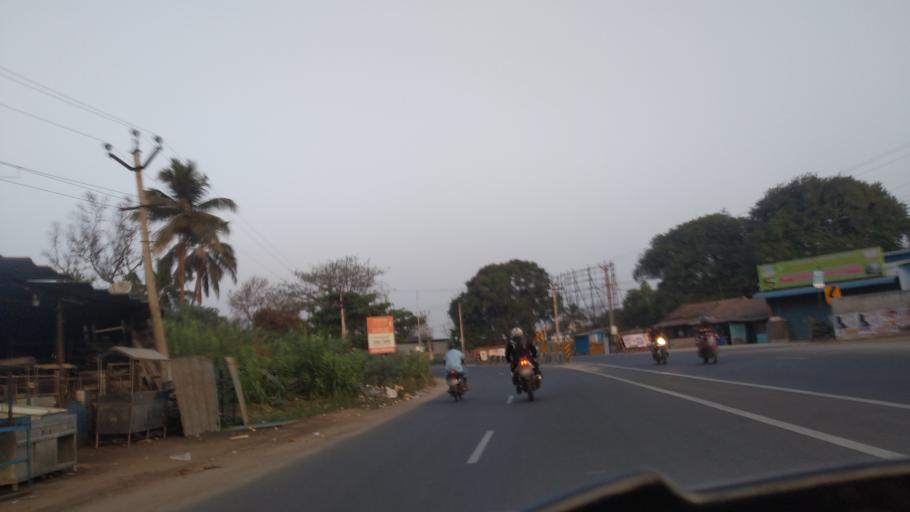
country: IN
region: Tamil Nadu
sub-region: Coimbatore
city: Coimbatore
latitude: 10.9725
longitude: 76.9652
